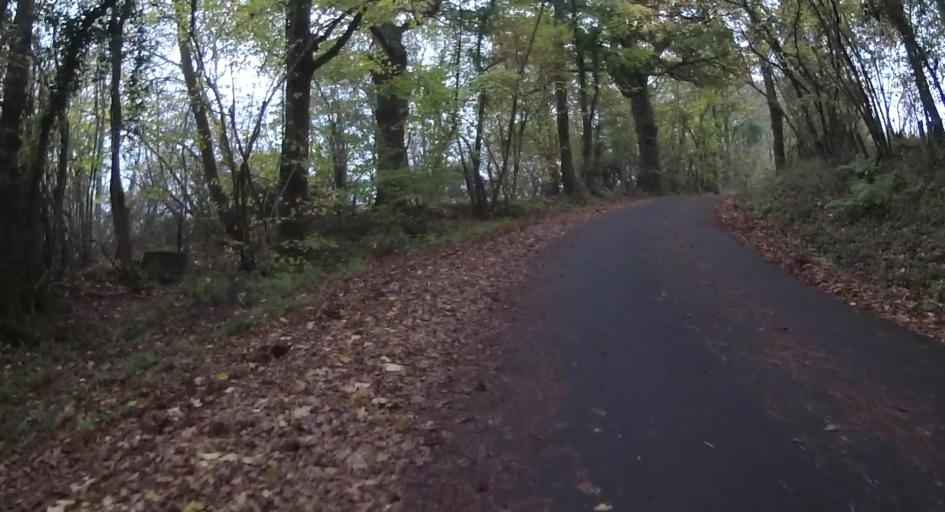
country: GB
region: England
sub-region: Surrey
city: Farnham
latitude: 51.1696
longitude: -0.8231
